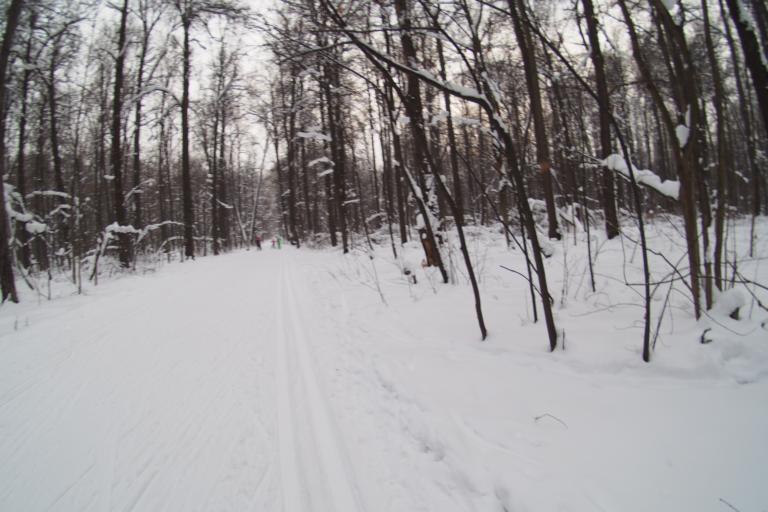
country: RU
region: Moskovskaya
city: Izmaylovo
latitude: 55.7691
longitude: 37.7774
